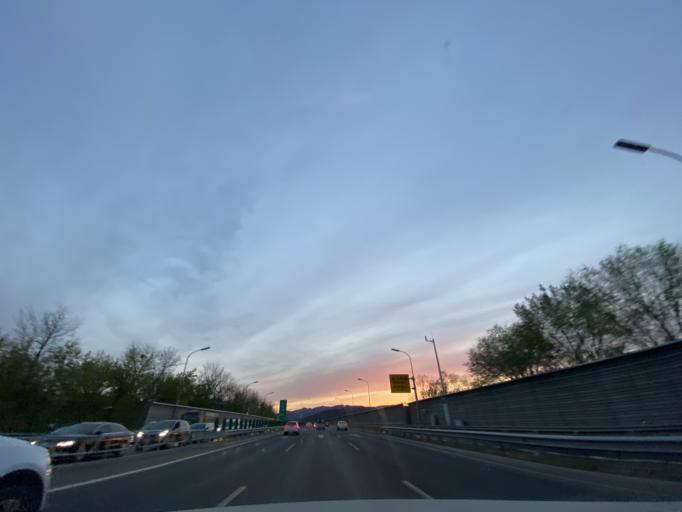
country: CN
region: Beijing
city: Haidian
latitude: 40.0114
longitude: 116.2740
